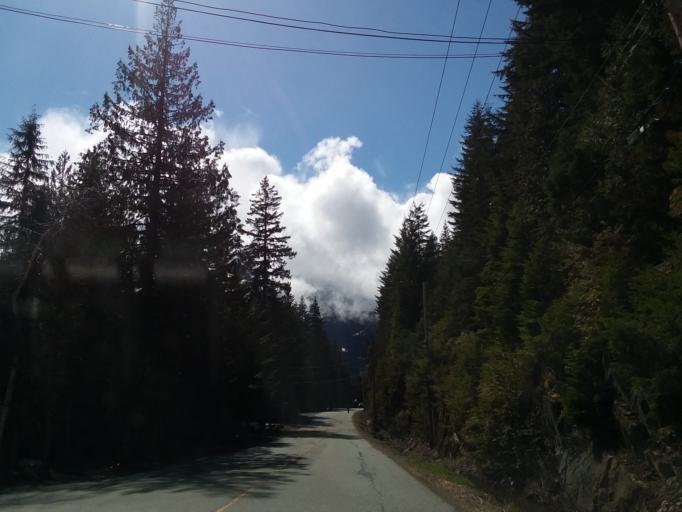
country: CA
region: British Columbia
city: Whistler
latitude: 50.1143
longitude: -122.9862
